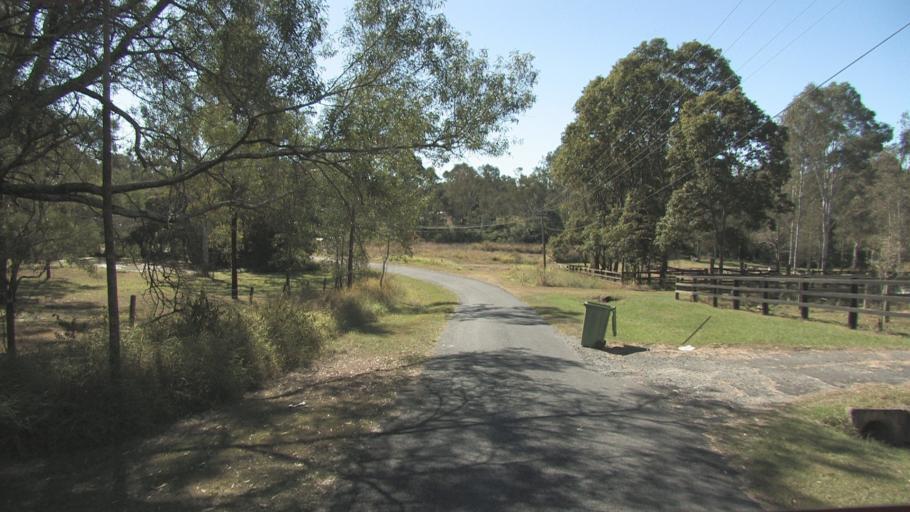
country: AU
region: Queensland
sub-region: Logan
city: North Maclean
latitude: -27.7655
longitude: 153.0297
